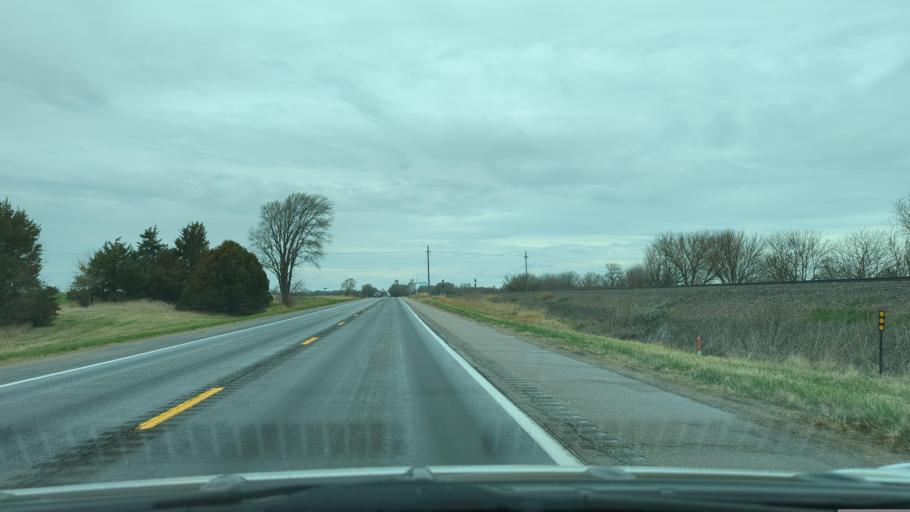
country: US
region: Nebraska
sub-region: Saunders County
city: Ashland
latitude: 40.9773
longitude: -96.4268
